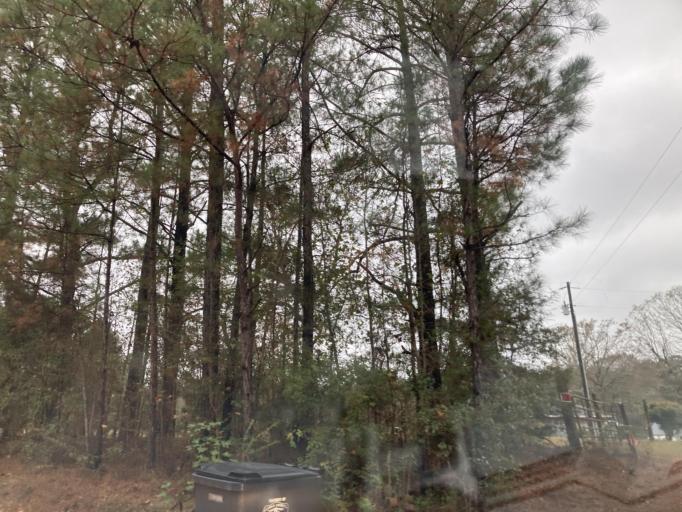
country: US
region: Mississippi
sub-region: Lamar County
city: Purvis
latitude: 31.1989
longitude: -89.4290
